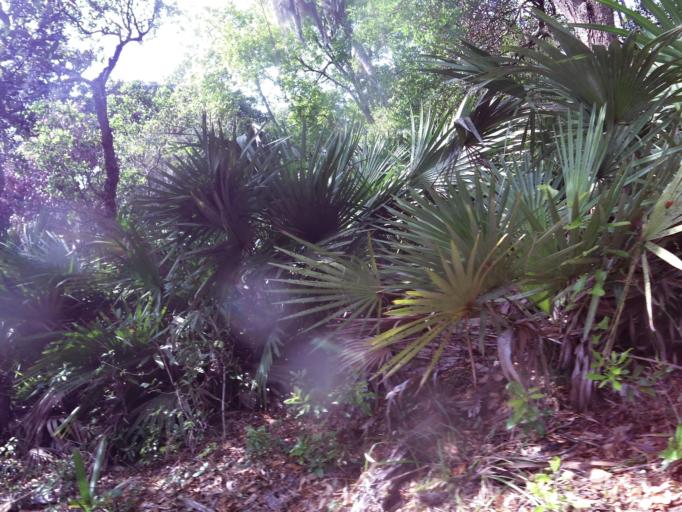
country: US
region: Florida
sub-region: Saint Johns County
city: Villano Beach
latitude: 30.0163
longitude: -81.3402
